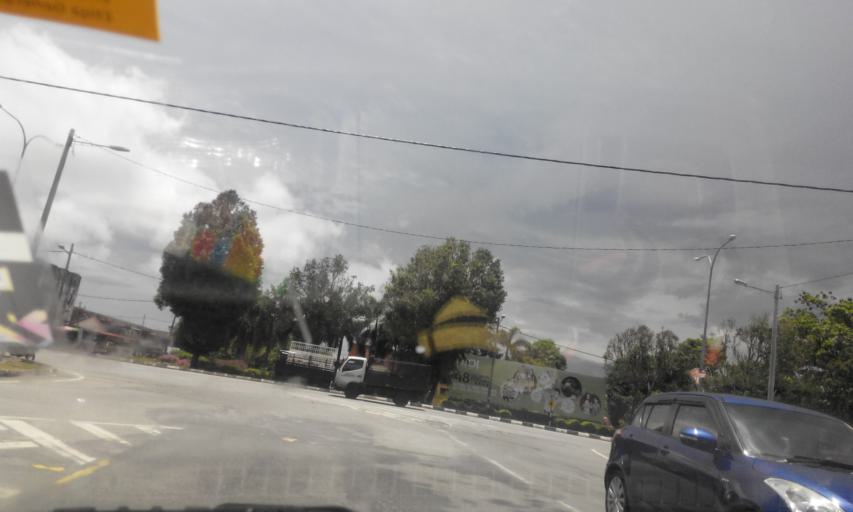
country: MY
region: Perak
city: Parit Buntar
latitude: 5.1194
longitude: 100.4864
